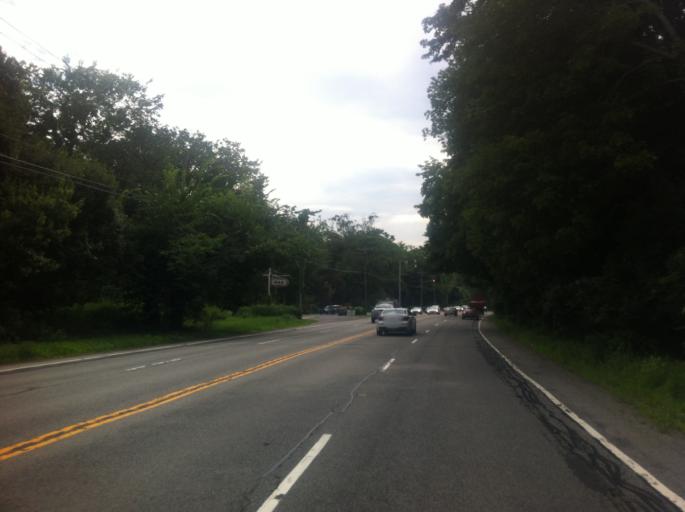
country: US
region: New York
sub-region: Nassau County
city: Upper Brookville
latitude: 40.8324
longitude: -73.5675
